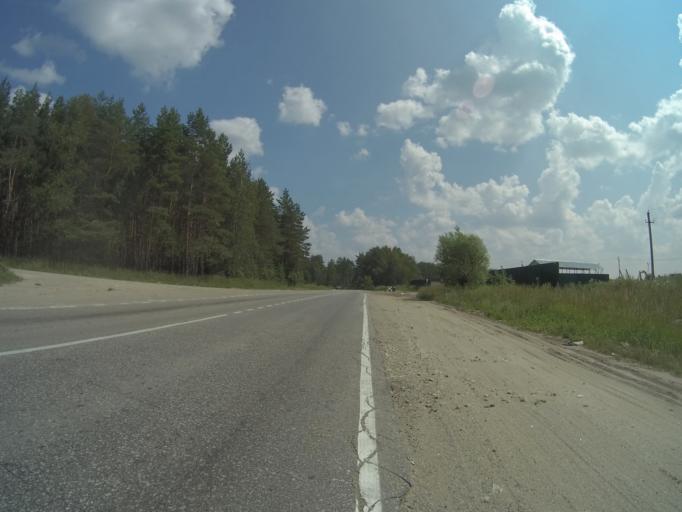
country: RU
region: Vladimir
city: Gus'-Khrustal'nyy
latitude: 55.6359
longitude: 40.7584
